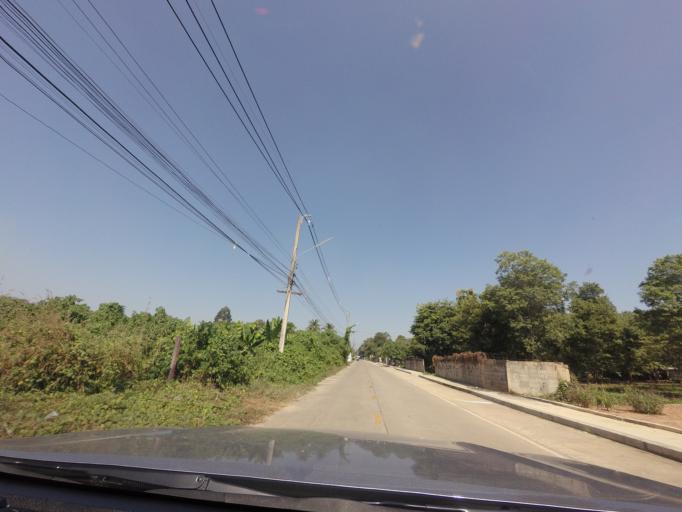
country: TH
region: Sukhothai
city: Sawankhalok
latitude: 17.3172
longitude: 99.8258
